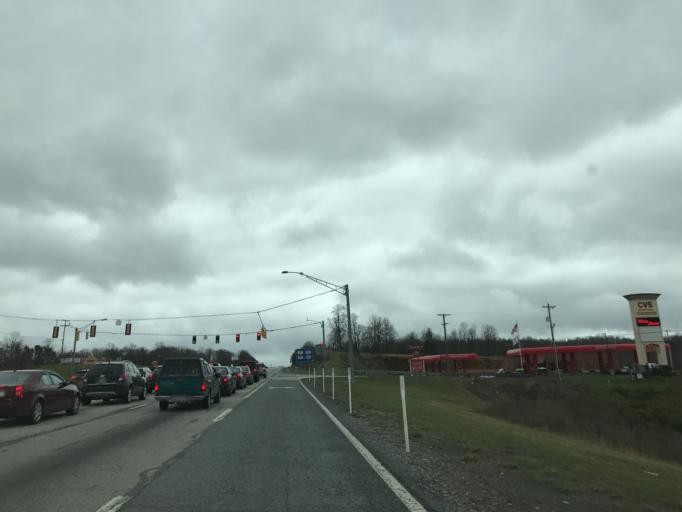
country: US
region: West Virginia
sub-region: Fayette County
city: Fayetteville
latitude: 38.0327
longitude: -81.1232
